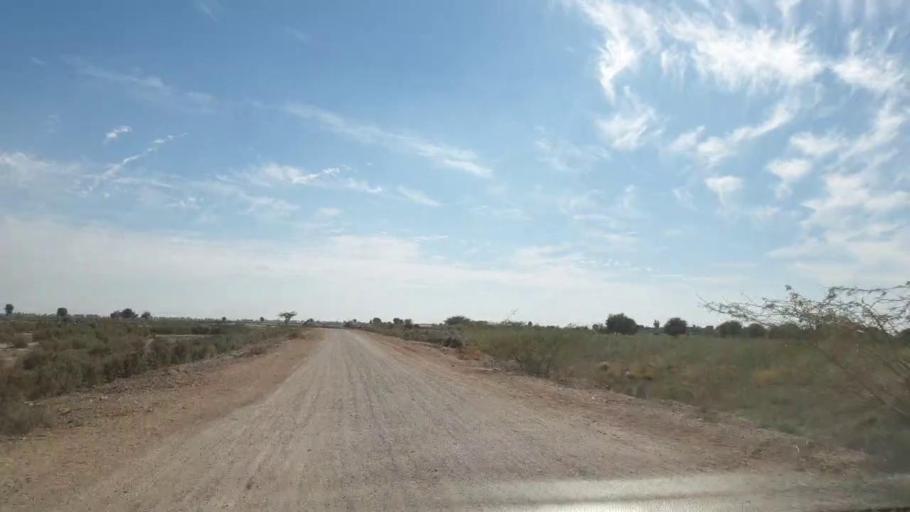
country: PK
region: Sindh
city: Pithoro
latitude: 25.5745
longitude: 69.3050
